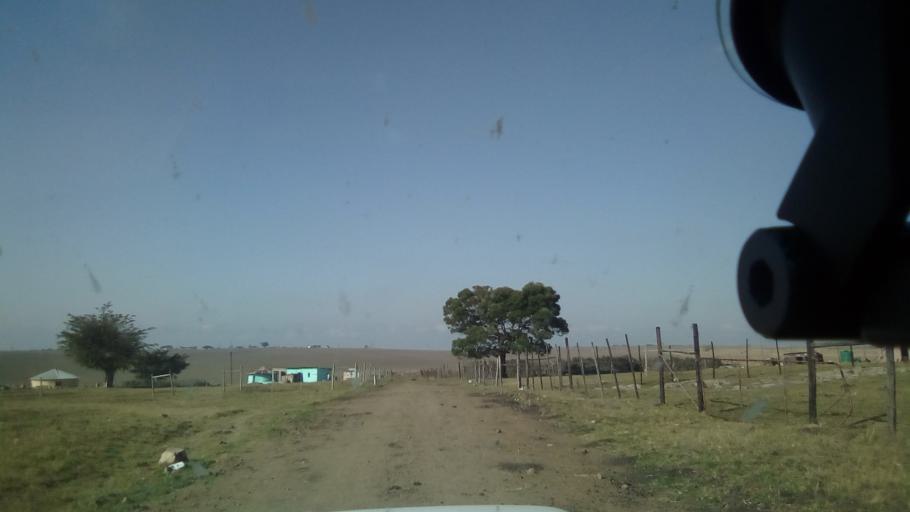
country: ZA
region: Eastern Cape
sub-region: Buffalo City Metropolitan Municipality
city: Bhisho
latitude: -32.9525
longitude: 27.3192
